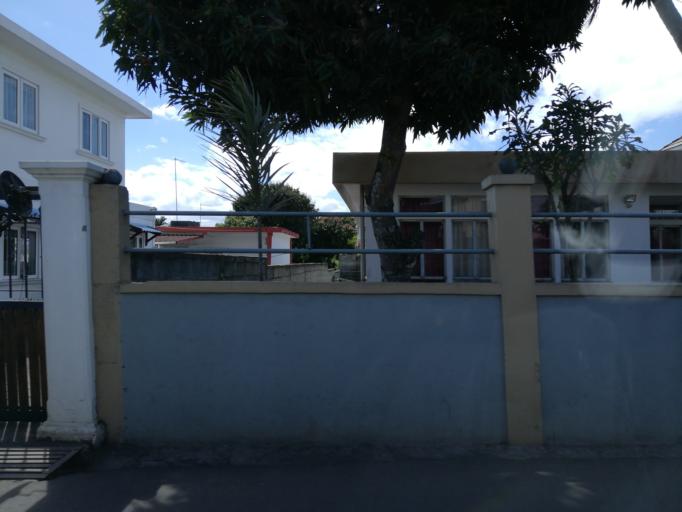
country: MU
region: Plaines Wilhems
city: Ebene
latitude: -20.2329
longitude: 57.4654
